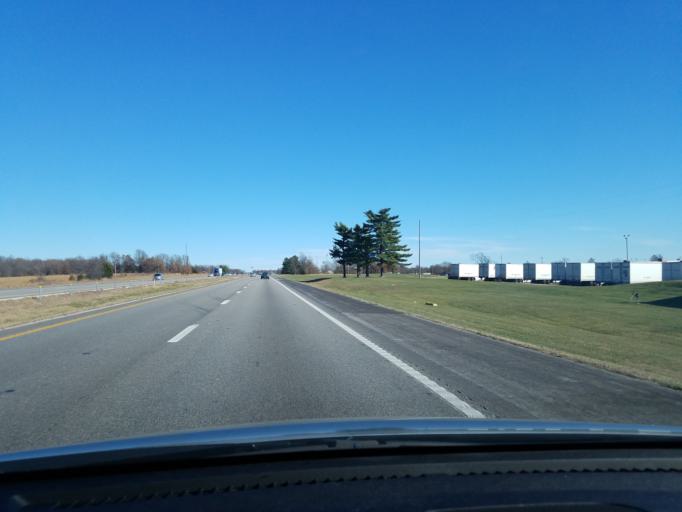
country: US
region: Missouri
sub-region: Greene County
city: Strafford
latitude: 37.2606
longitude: -93.1526
